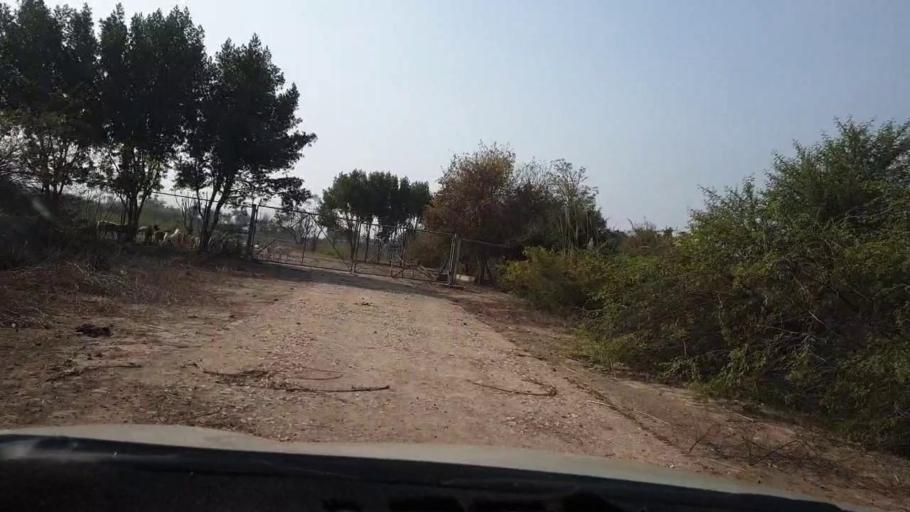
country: PK
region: Sindh
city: Matiari
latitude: 25.6222
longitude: 68.4983
